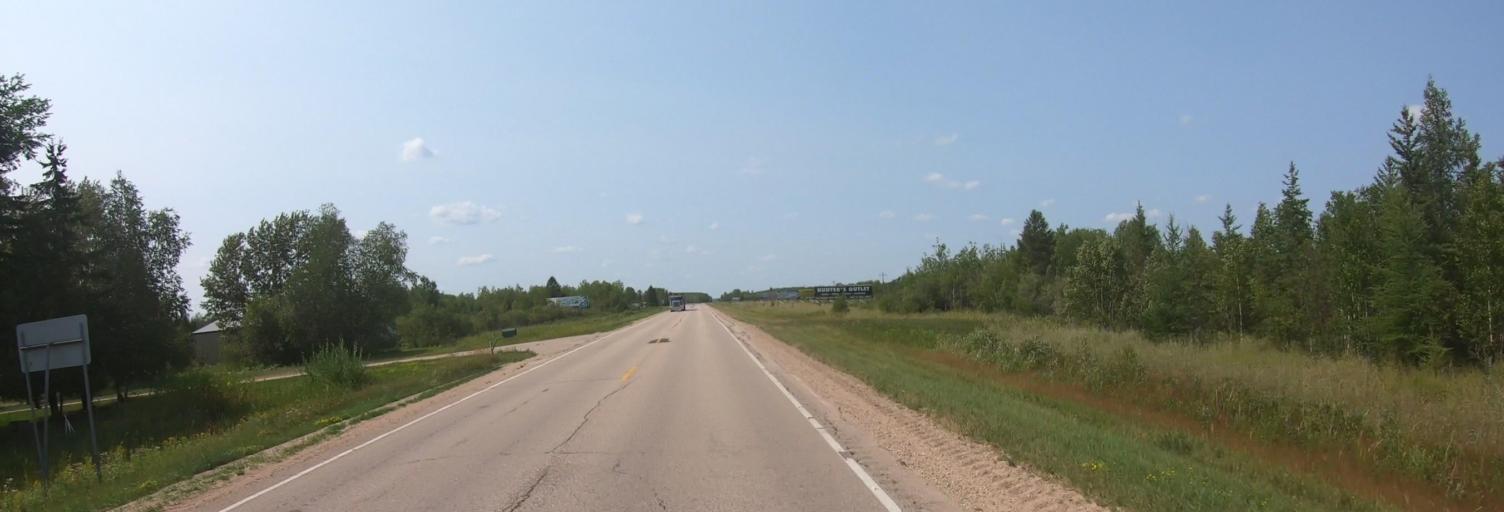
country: US
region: Minnesota
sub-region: Lake of the Woods County
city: Baudette
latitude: 48.7404
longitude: -94.8399
